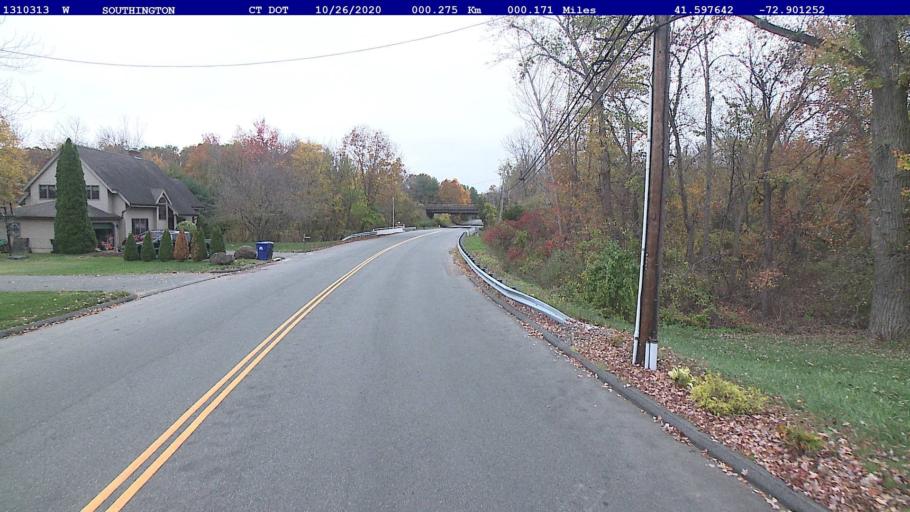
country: US
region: Connecticut
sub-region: New Haven County
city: Wolcott
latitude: 41.5976
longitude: -72.9013
